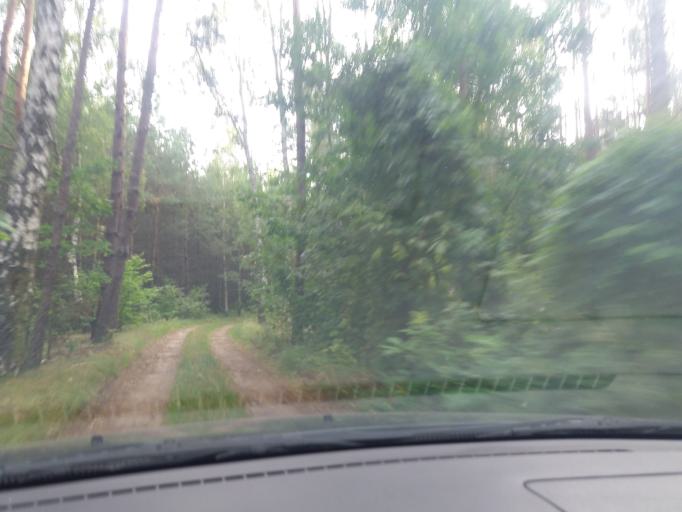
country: PL
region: Masovian Voivodeship
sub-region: Powiat mlawski
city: Wieczfnia Koscielna
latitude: 53.2200
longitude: 20.4589
